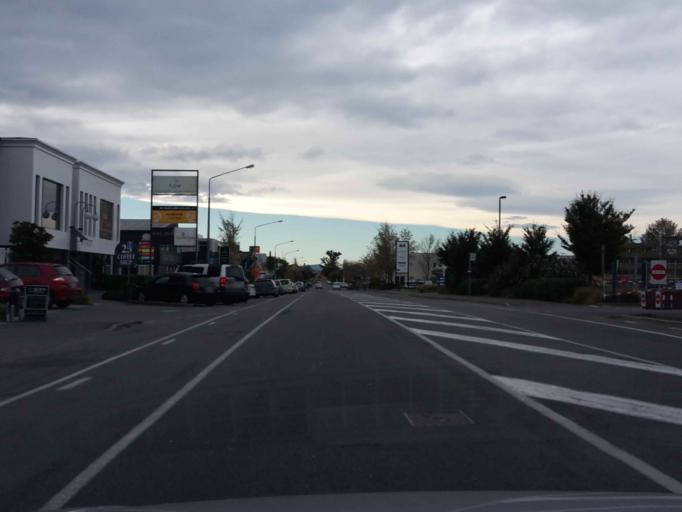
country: NZ
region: Canterbury
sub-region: Christchurch City
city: Christchurch
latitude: -43.5359
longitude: 172.6070
